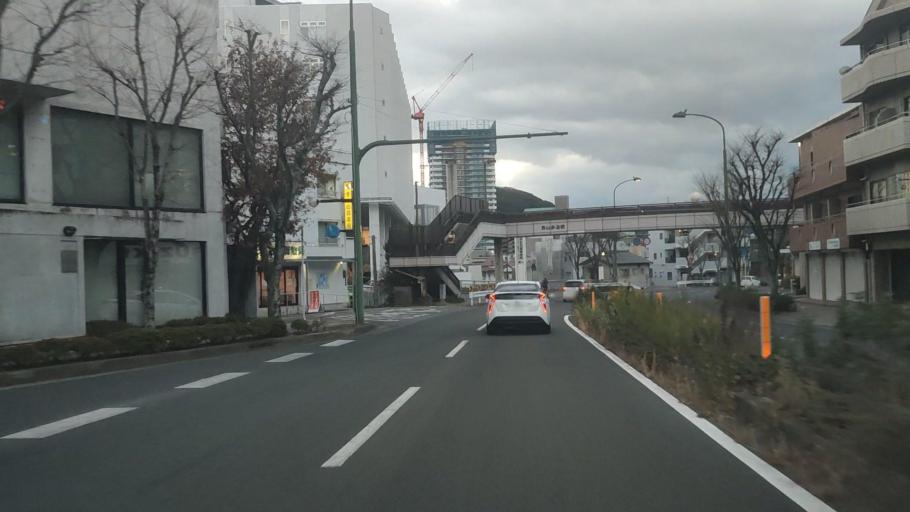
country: JP
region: Nagasaki
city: Nagasaki-shi
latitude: 32.7572
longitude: 129.8866
